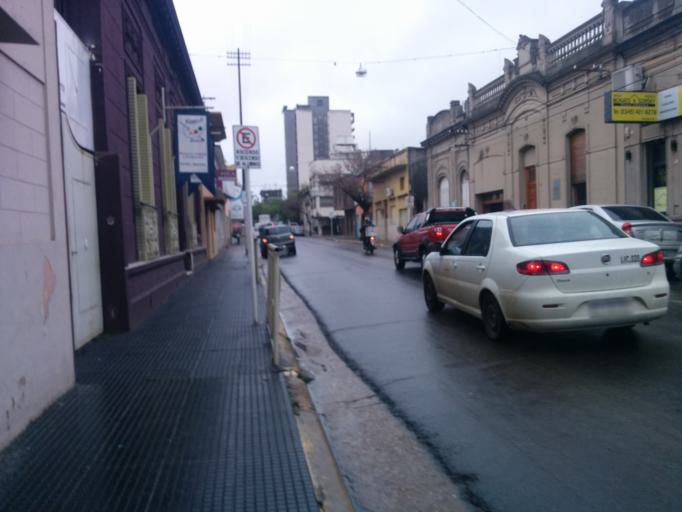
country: AR
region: Entre Rios
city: Concordia
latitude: -31.3948
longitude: -58.0150
